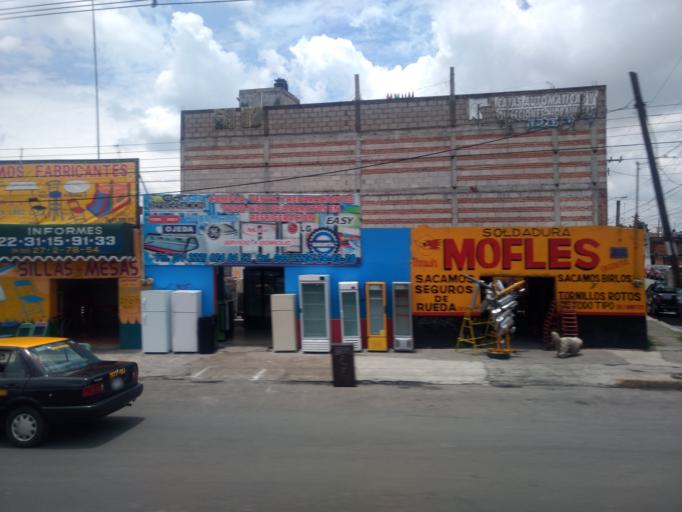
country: MX
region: Puebla
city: Puebla
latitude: 19.0804
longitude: -98.2043
